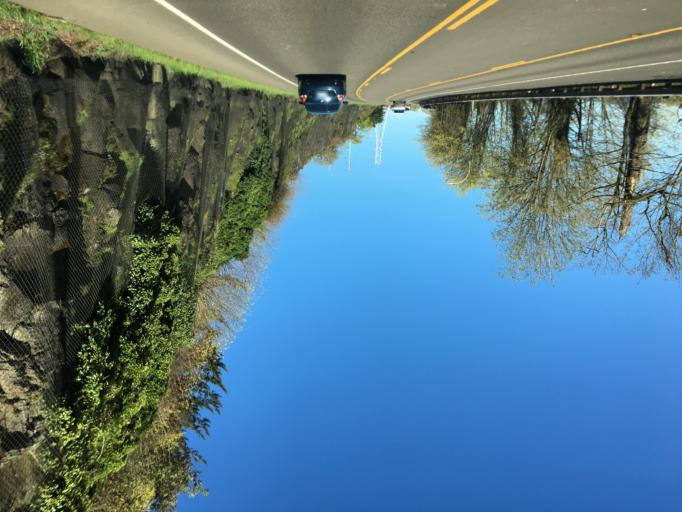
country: US
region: Oregon
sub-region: Clackamas County
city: Oregon City
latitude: 45.3482
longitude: -122.6187
